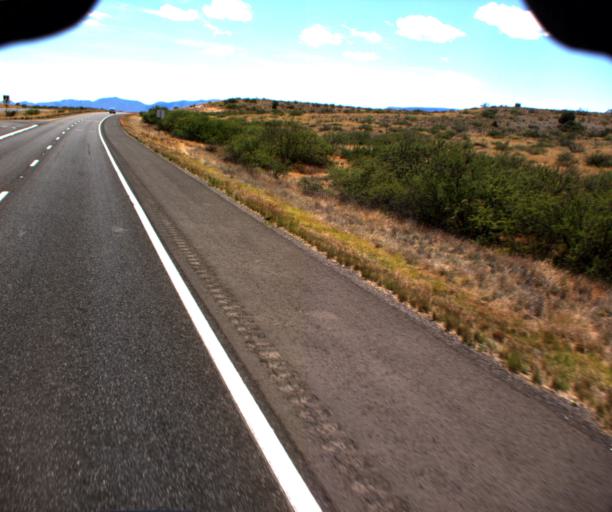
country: US
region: Arizona
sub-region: Yavapai County
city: Cornville
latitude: 34.7789
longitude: -111.9280
